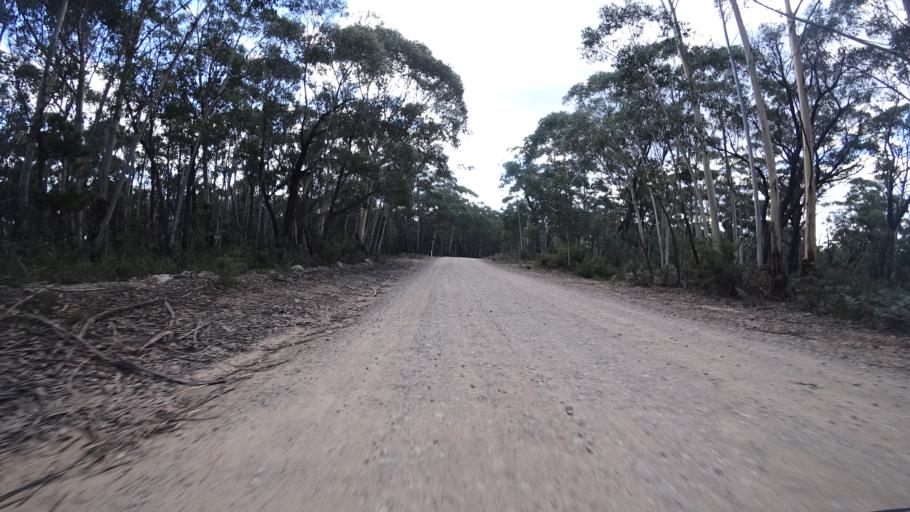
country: AU
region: New South Wales
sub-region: Lithgow
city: Lithgow
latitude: -33.3937
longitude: 150.2189
